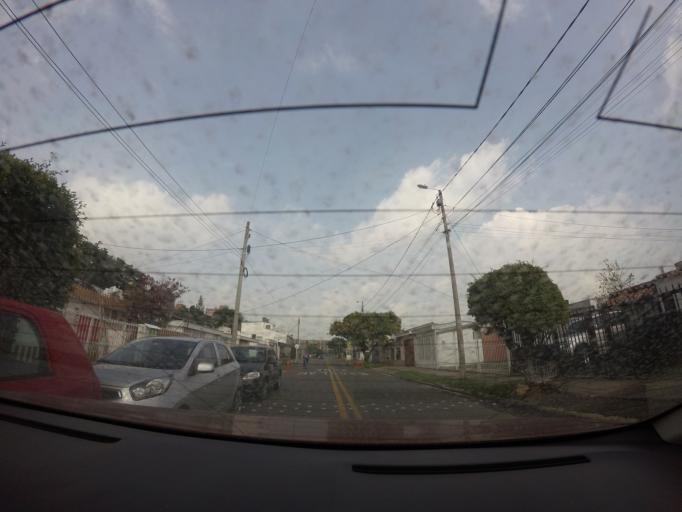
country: CO
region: Bogota D.C.
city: Barrio San Luis
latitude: 4.7106
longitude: -74.0571
